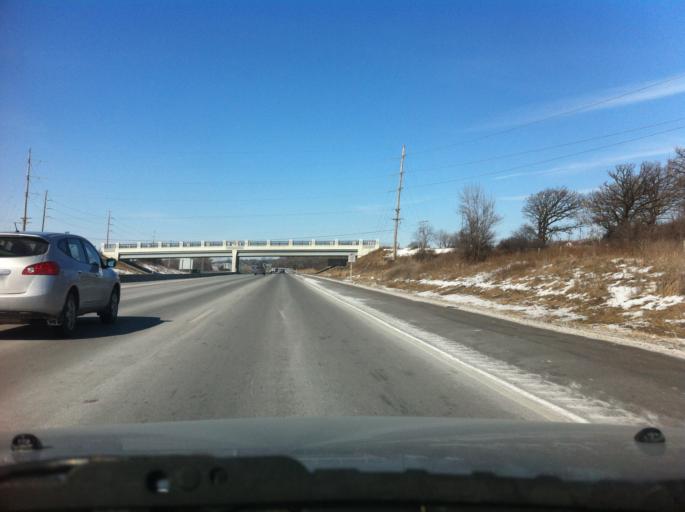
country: US
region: Wisconsin
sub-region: Dane County
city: Monona
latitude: 43.1382
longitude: -89.2965
